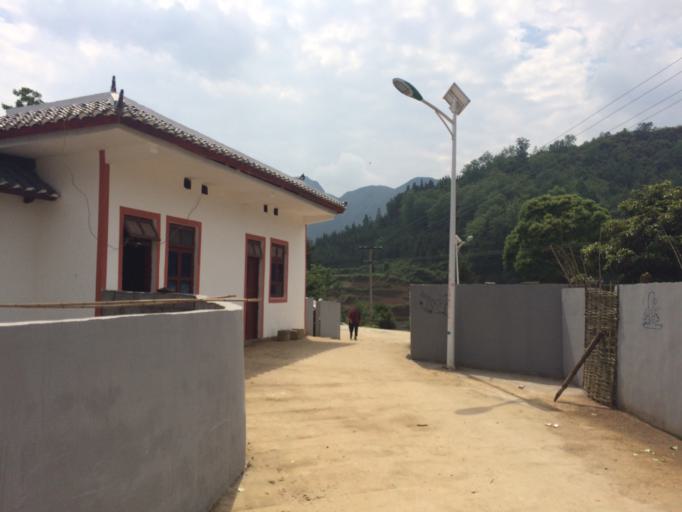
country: CN
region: Guangxi Zhuangzu Zizhiqu
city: Xinzhou
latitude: 25.6293
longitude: 105.2664
